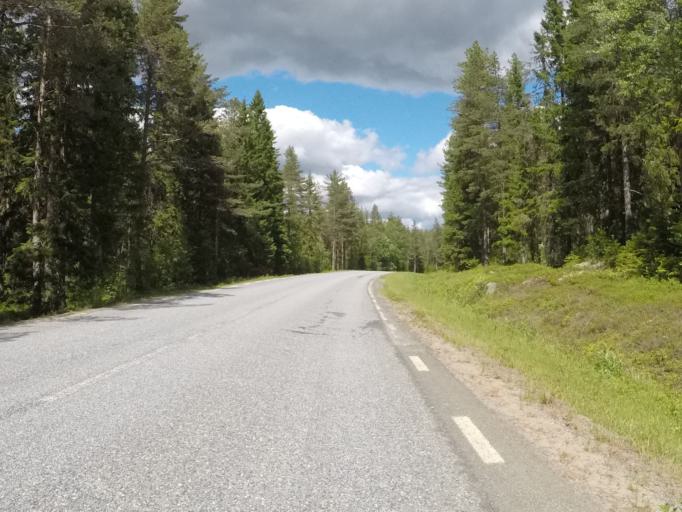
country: SE
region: Vaesterbotten
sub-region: Robertsfors Kommun
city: Robertsfors
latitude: 63.9757
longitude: 20.8099
